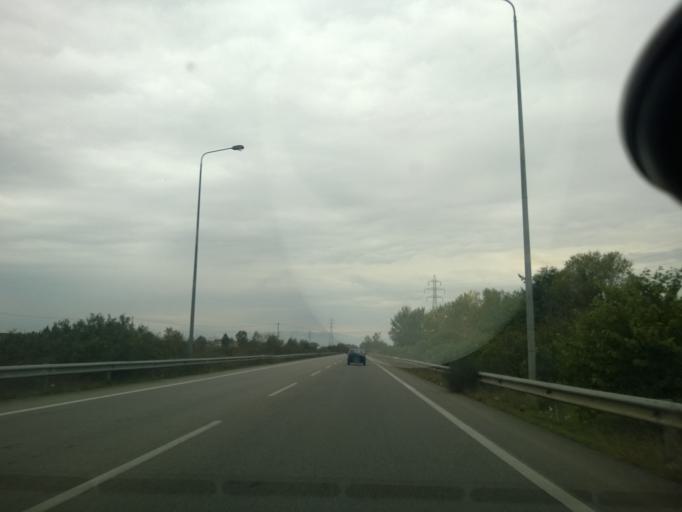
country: GR
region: Central Macedonia
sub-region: Nomos Pellis
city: Melissi
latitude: 40.7779
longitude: 22.3546
